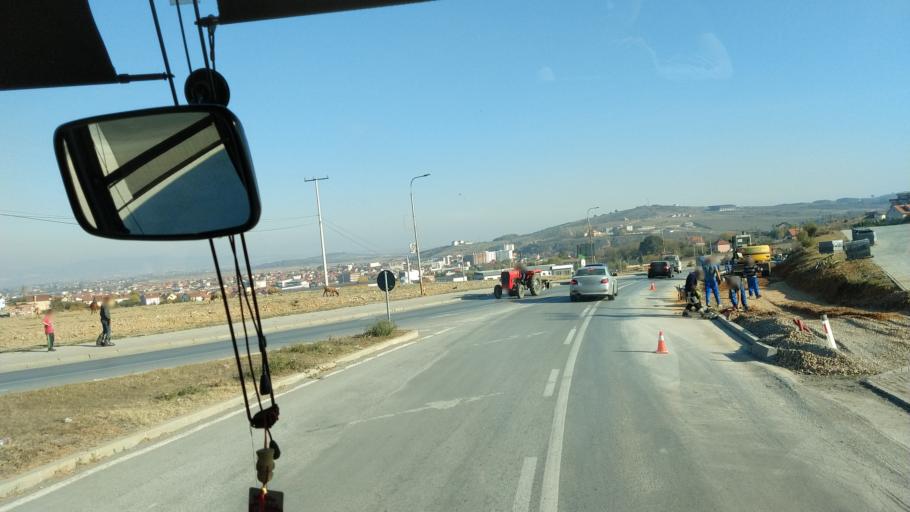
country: XK
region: Ferizaj
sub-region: Komuna e Shtimes
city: Shtime
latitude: 42.4374
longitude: 21.0227
